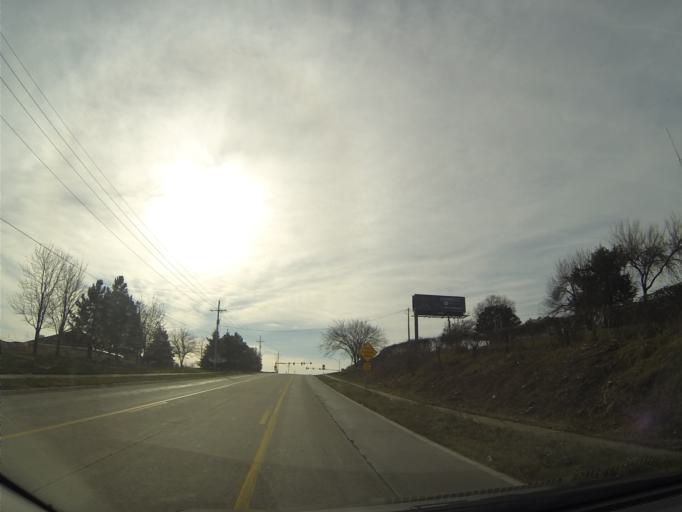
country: US
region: Nebraska
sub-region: Douglas County
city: Elkhorn
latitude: 41.2683
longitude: -96.2156
